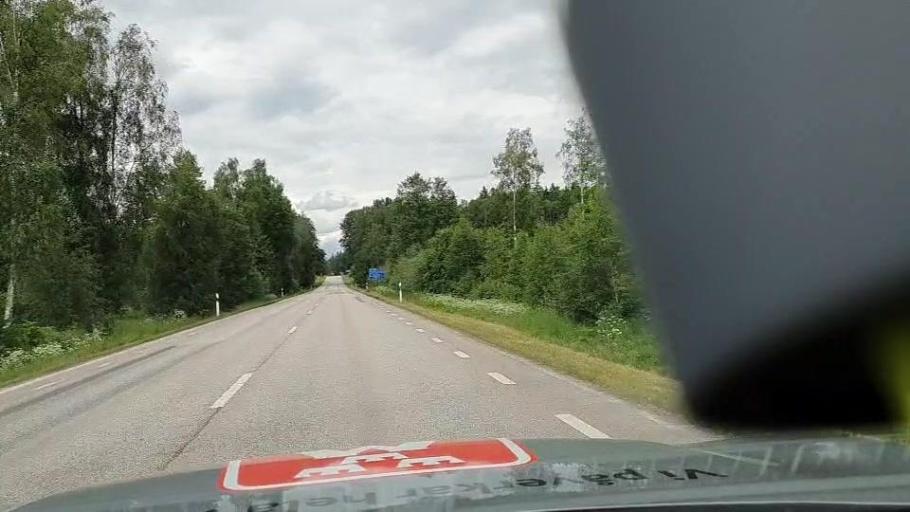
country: SE
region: Kalmar
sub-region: Emmaboda Kommun
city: Emmaboda
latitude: 56.5137
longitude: 15.6080
